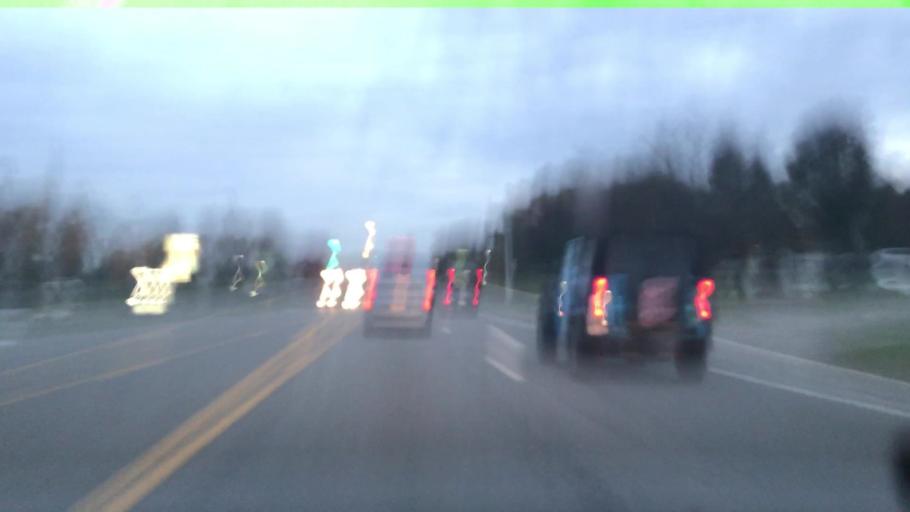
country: US
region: Michigan
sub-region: Oakland County
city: Bloomfield Hills
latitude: 42.6251
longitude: -83.2489
